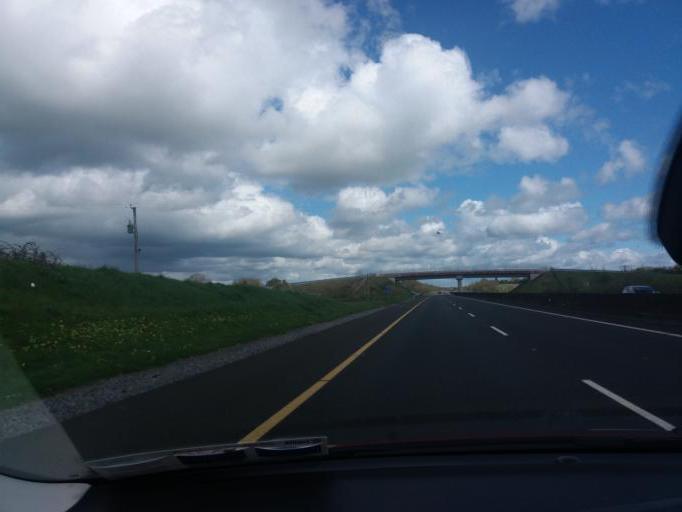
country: IE
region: Leinster
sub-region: Laois
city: Rathdowney
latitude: 52.7884
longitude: -7.5240
